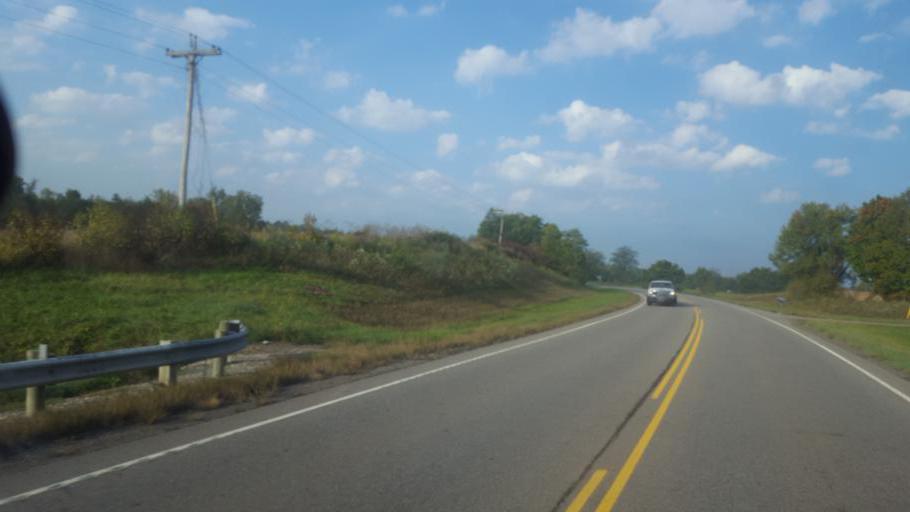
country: US
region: Ohio
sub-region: Licking County
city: Utica
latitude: 40.2274
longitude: -82.5306
